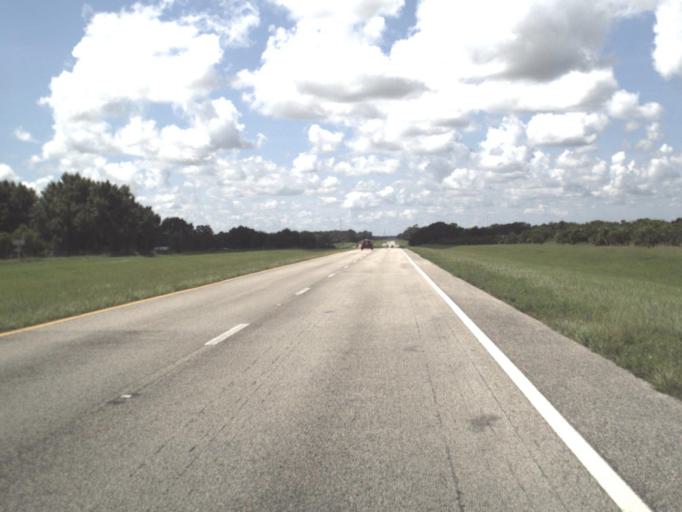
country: US
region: Florida
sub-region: DeSoto County
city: Arcadia
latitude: 27.2939
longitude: -81.8259
